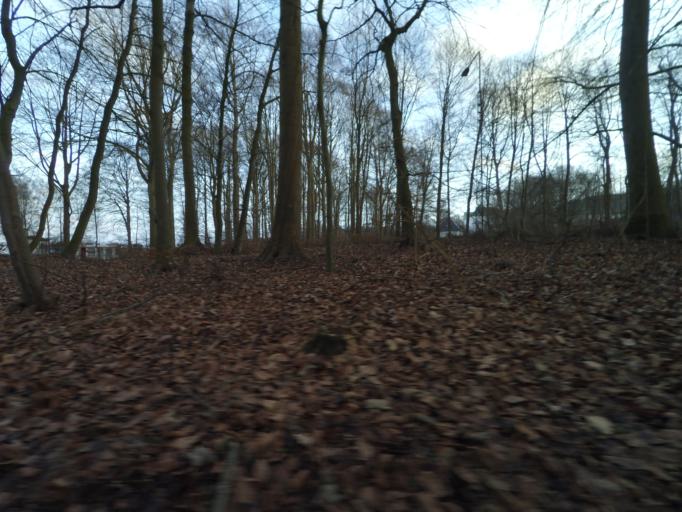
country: DK
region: Central Jutland
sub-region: Arhus Kommune
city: Arhus
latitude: 56.1294
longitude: 10.2011
